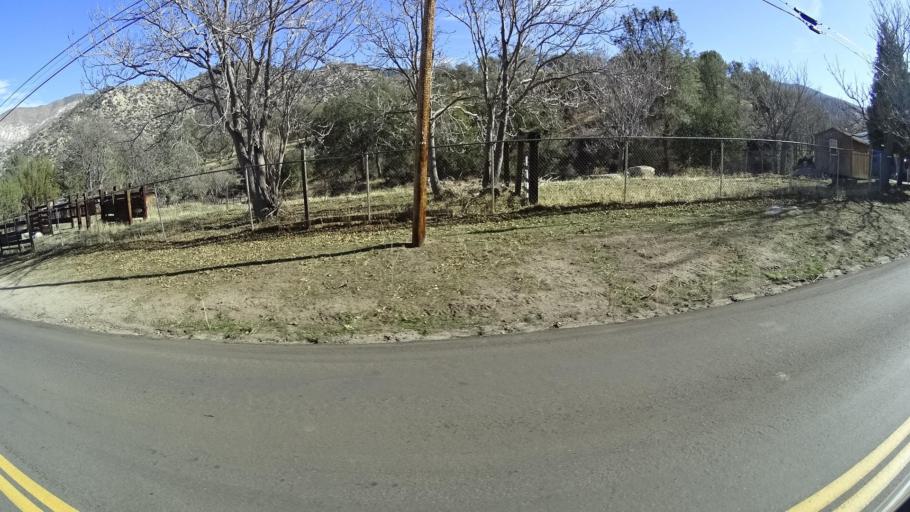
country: US
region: California
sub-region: Kern County
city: Bodfish
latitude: 35.5171
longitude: -118.5178
